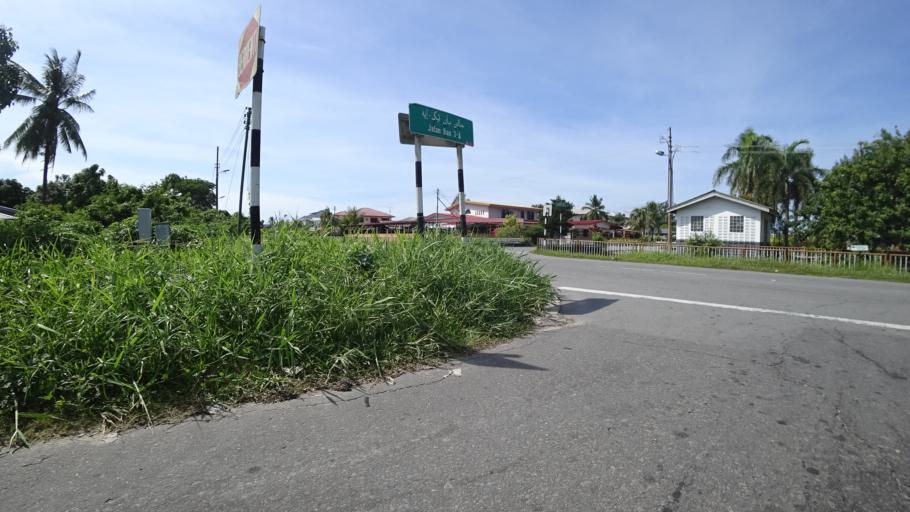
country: BN
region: Brunei and Muara
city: Bandar Seri Begawan
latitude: 4.8840
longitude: 114.8491
